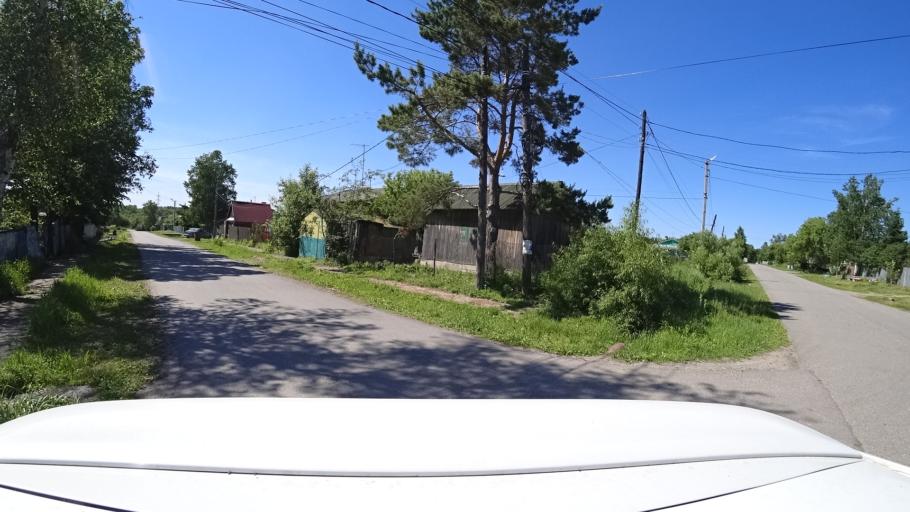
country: RU
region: Khabarovsk Krai
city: Topolevo
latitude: 48.5567
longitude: 135.1899
